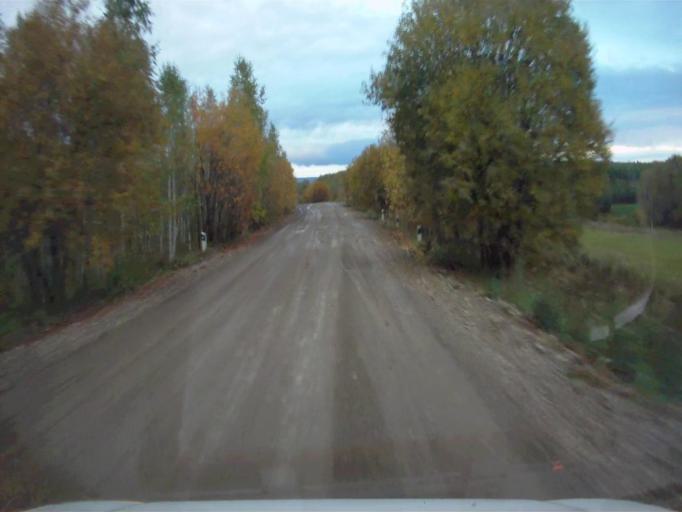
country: RU
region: Sverdlovsk
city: Mikhaylovsk
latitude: 56.2079
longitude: 59.2075
